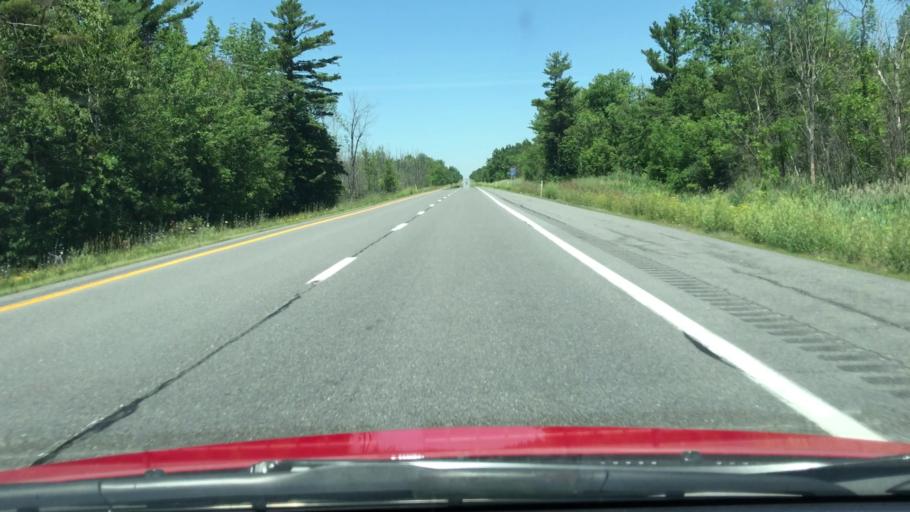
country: US
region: New York
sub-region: Clinton County
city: Champlain
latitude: 44.9407
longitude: -73.4472
